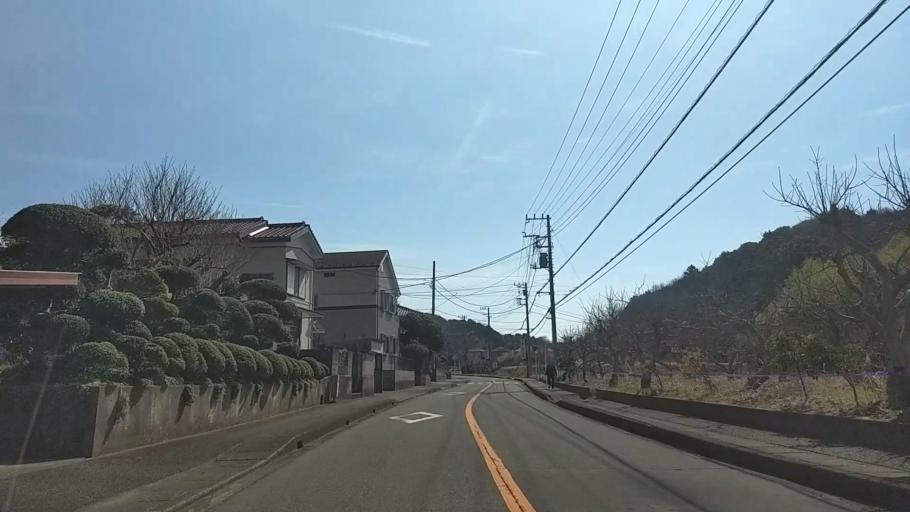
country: JP
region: Kanagawa
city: Fujisawa
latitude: 35.3780
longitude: 139.4286
